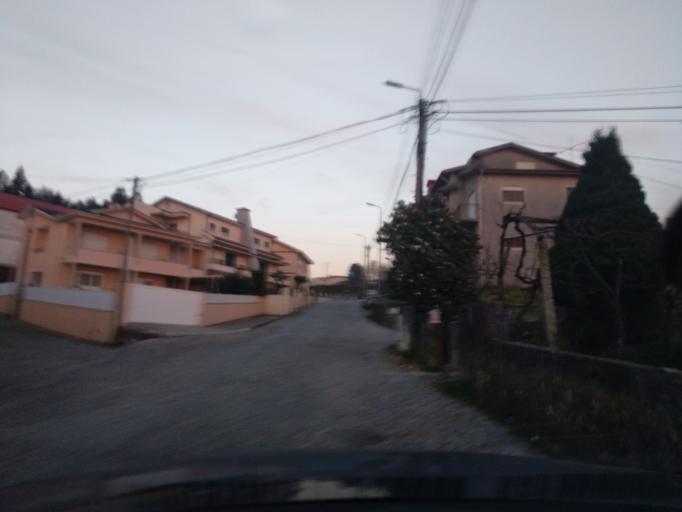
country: PT
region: Porto
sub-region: Paredes
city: Lordelo
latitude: 41.2344
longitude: -8.4038
